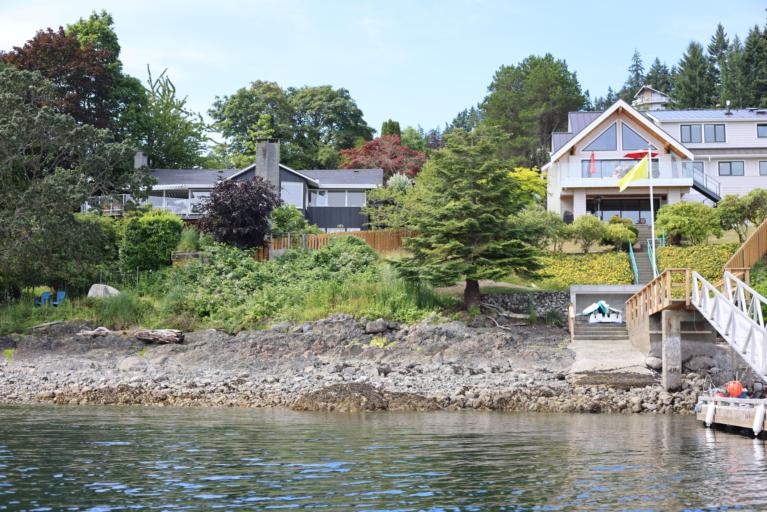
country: CA
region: British Columbia
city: Nanaimo
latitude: 49.2094
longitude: -123.9596
